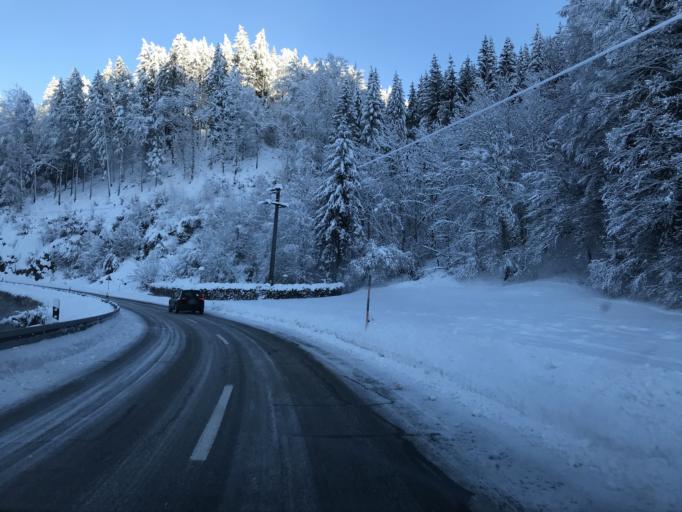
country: DE
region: Baden-Wuerttemberg
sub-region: Freiburg Region
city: Bollen
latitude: 47.7635
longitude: 7.8281
